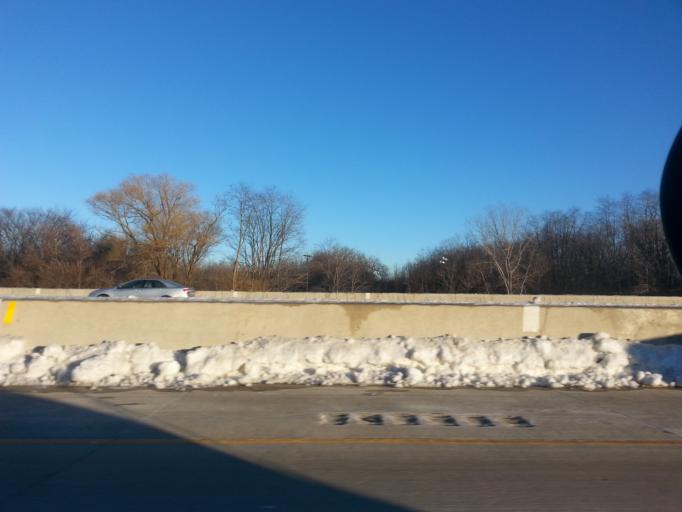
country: US
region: Wisconsin
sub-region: Kenosha County
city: Pleasant Prairie
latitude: 42.5137
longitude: -87.9518
